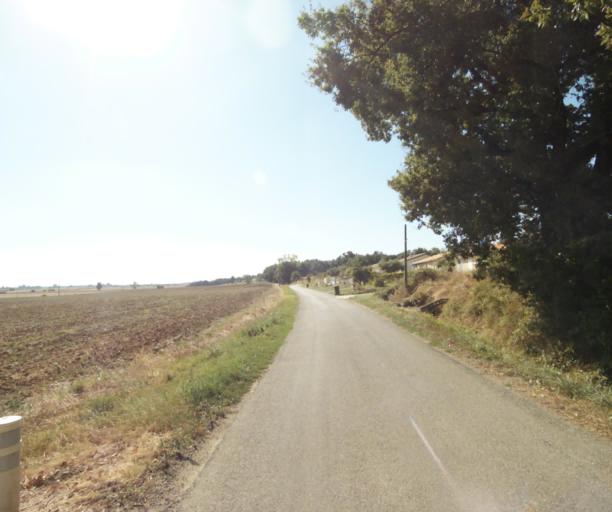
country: FR
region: Midi-Pyrenees
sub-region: Departement du Tarn-et-Garonne
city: Verdun-sur-Garonne
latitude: 43.8328
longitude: 1.2047
